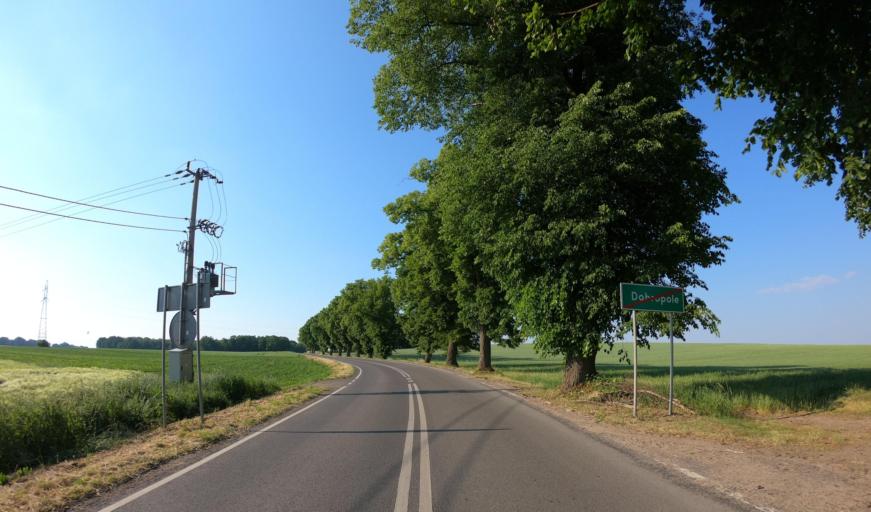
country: PL
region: West Pomeranian Voivodeship
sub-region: Powiat lobeski
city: Dobra
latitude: 53.5352
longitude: 15.3149
